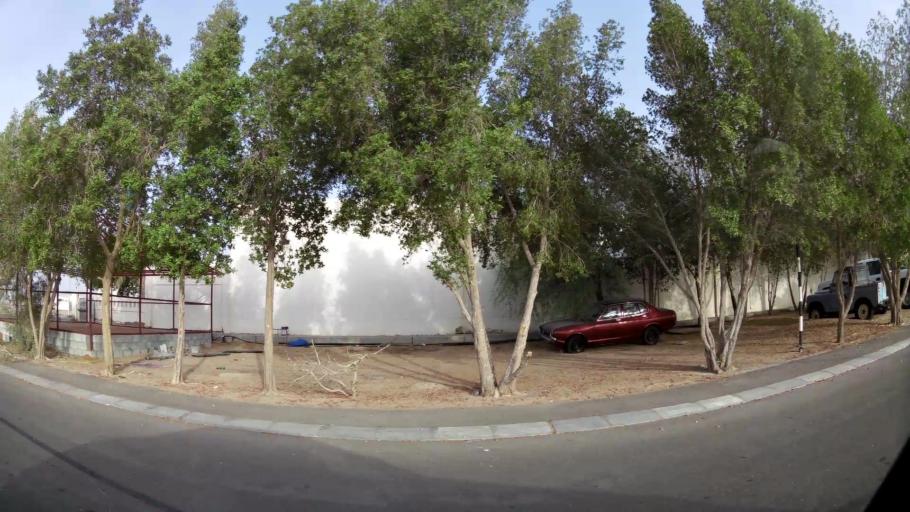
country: AE
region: Abu Dhabi
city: Al Ain
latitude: 24.1043
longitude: 55.7100
